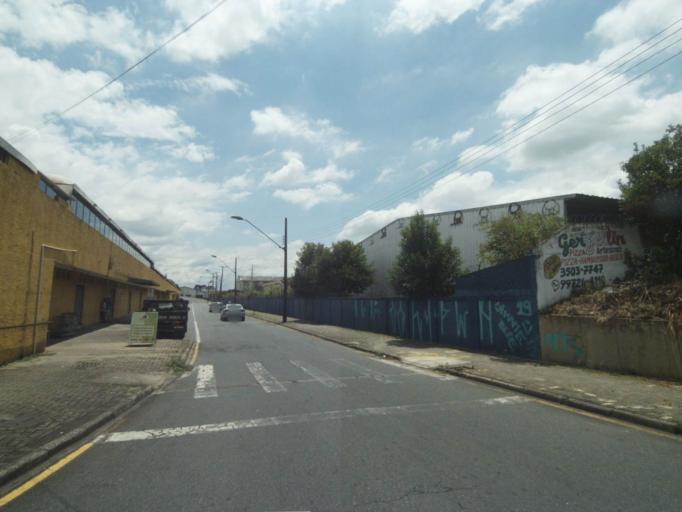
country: BR
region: Parana
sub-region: Pinhais
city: Pinhais
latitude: -25.4523
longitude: -49.2145
